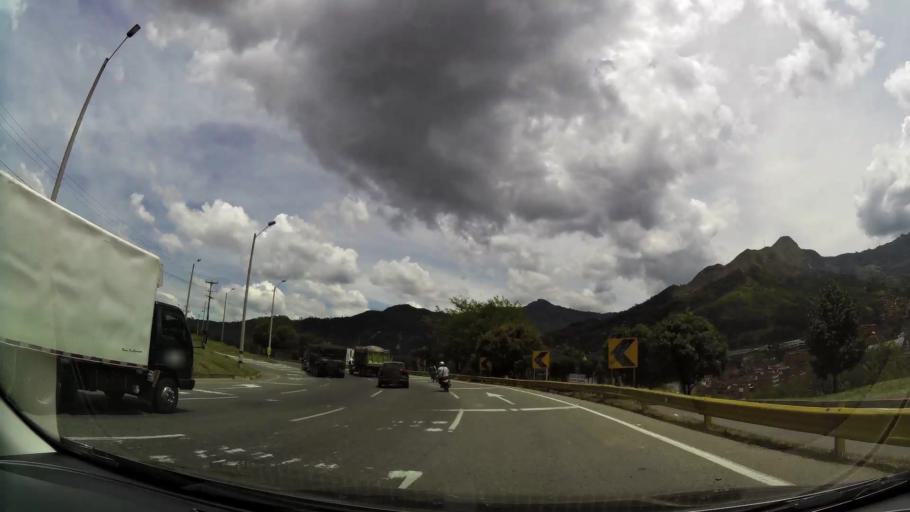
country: CO
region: Antioquia
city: Municipio de Copacabana
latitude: 6.3504
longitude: -75.5098
